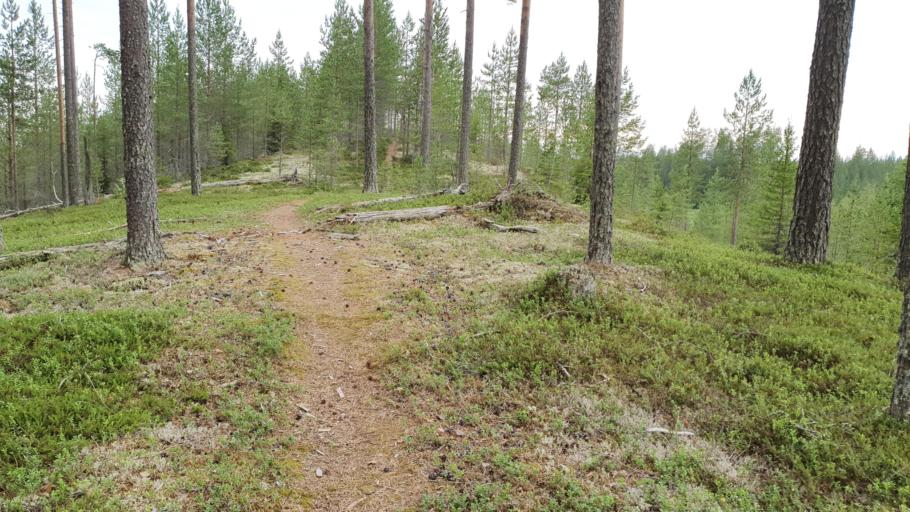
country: RU
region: Republic of Karelia
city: Kostomuksha
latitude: 64.7566
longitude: 29.9961
